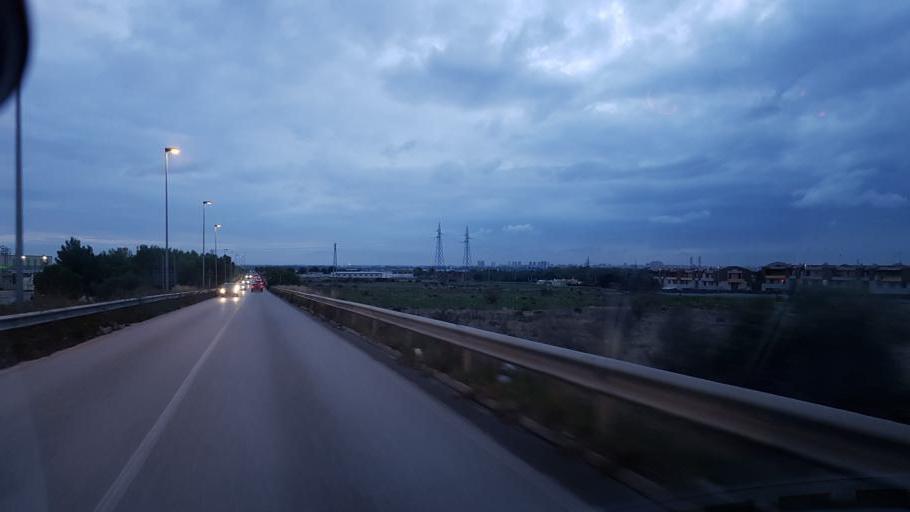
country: IT
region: Apulia
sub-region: Provincia di Taranto
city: Paolo VI
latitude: 40.5182
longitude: 17.2875
